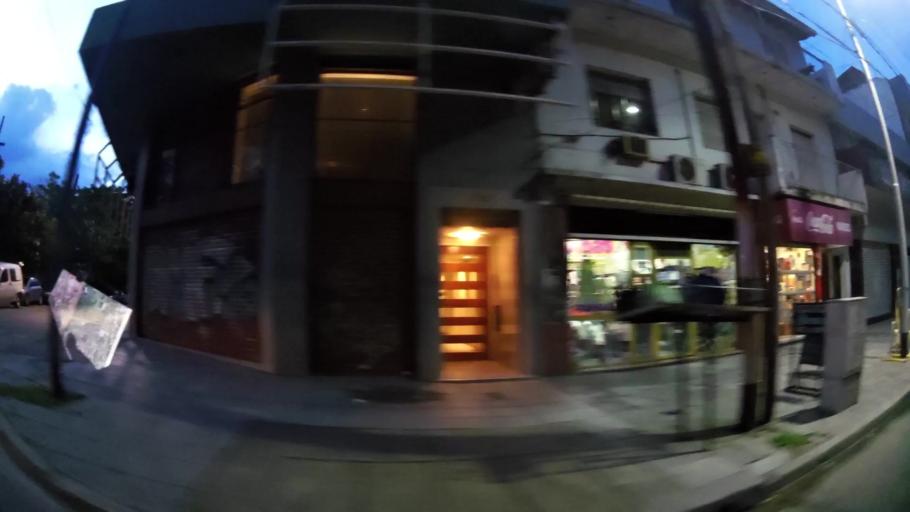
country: AR
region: Buenos Aires
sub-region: Partido de Quilmes
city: Quilmes
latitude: -34.6976
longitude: -58.3100
